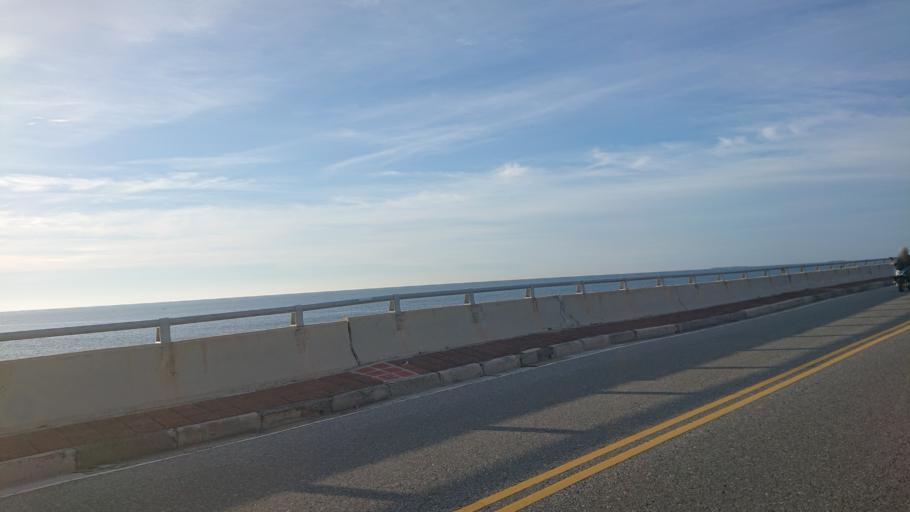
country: TW
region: Taiwan
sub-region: Penghu
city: Ma-kung
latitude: 23.6422
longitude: 119.5417
